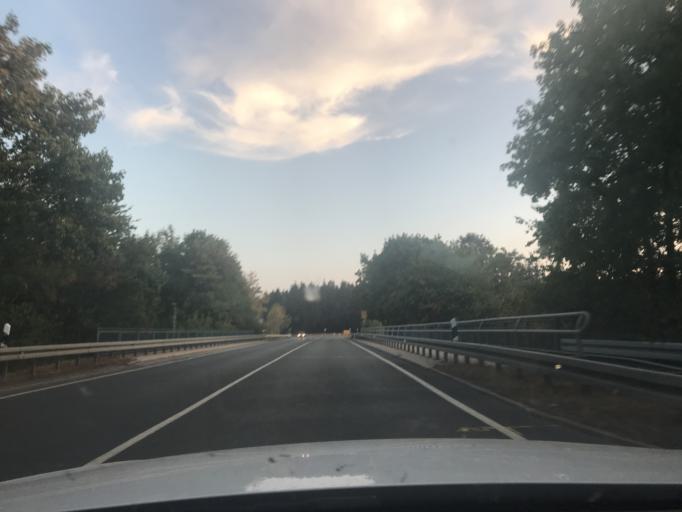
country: DE
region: Bavaria
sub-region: Upper Franconia
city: Emtmannsberg
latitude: 49.8860
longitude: 11.6112
